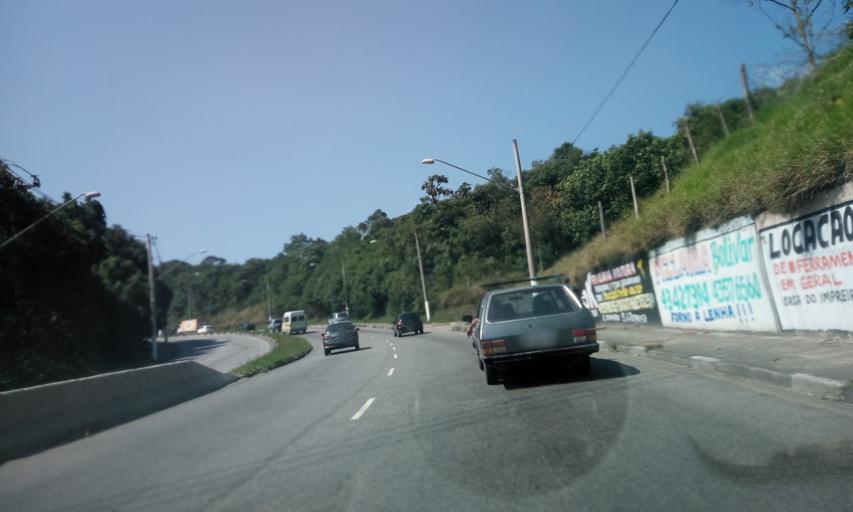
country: BR
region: Sao Paulo
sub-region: Sao Bernardo Do Campo
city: Sao Bernardo do Campo
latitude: -23.7507
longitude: -46.5706
